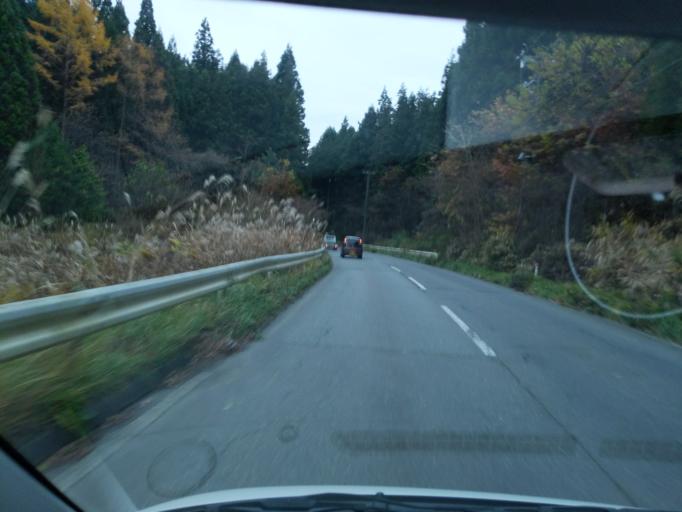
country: JP
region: Iwate
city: Mizusawa
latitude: 39.0260
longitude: 141.3331
